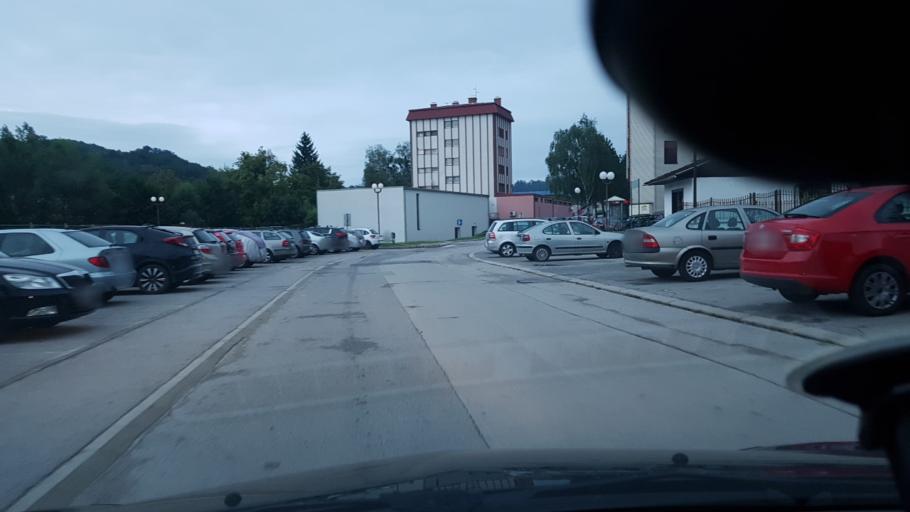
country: SI
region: Rogatec
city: Rogatec
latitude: 46.2227
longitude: 15.6978
